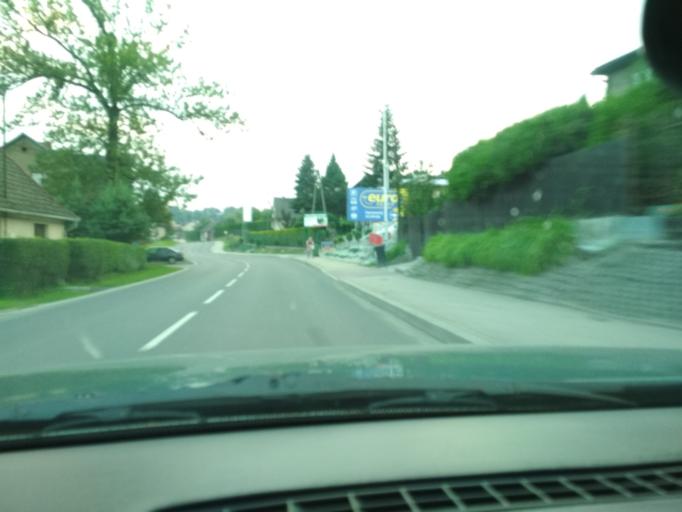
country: PL
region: Silesian Voivodeship
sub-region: Powiat bielski
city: Jasienica
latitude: 49.8417
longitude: 18.9407
